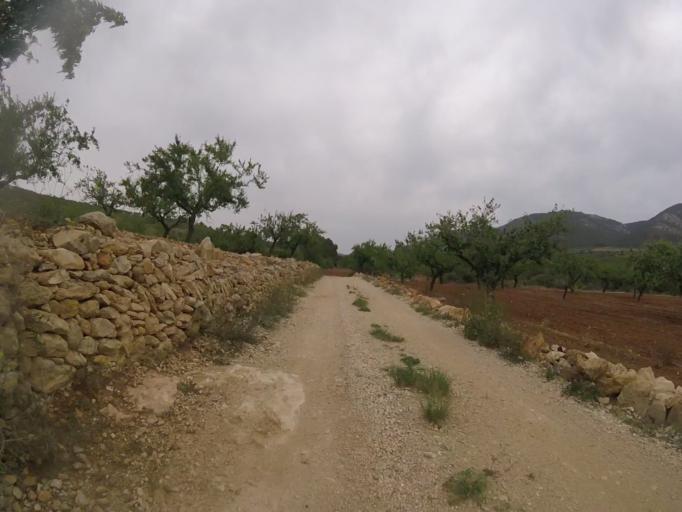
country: ES
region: Valencia
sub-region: Provincia de Castello
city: Alcala de Xivert
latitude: 40.2882
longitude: 0.2587
